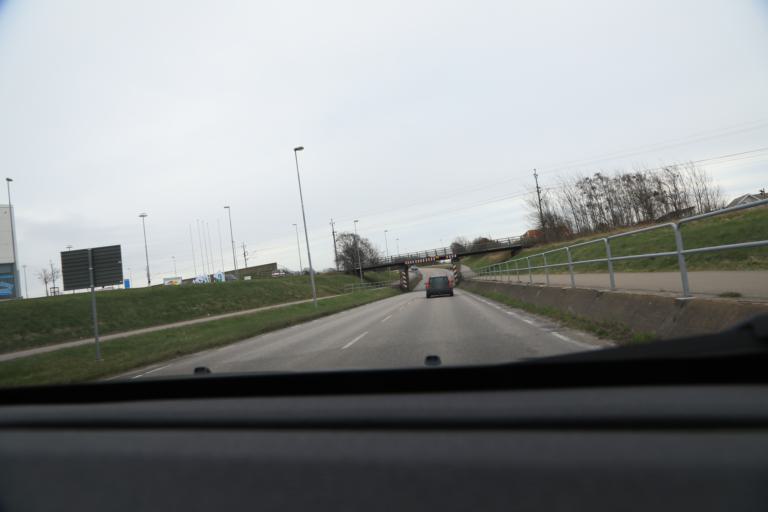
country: SE
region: Halland
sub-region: Varbergs Kommun
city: Traslovslage
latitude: 57.0825
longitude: 12.2759
